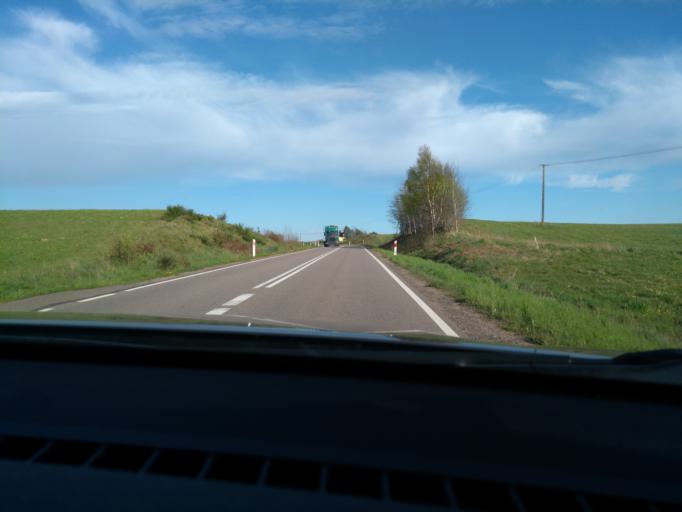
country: PL
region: Pomeranian Voivodeship
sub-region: Powiat leborski
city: Cewice
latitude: 54.3346
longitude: 17.7118
